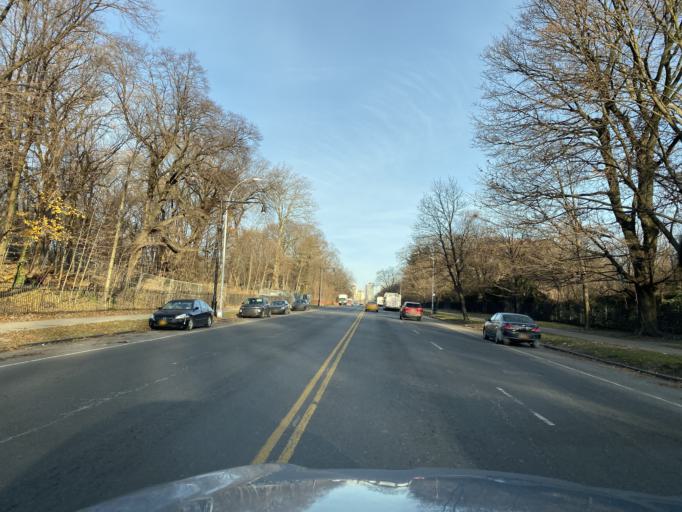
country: US
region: New York
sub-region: Kings County
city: Brooklyn
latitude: 40.6678
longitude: -73.9656
